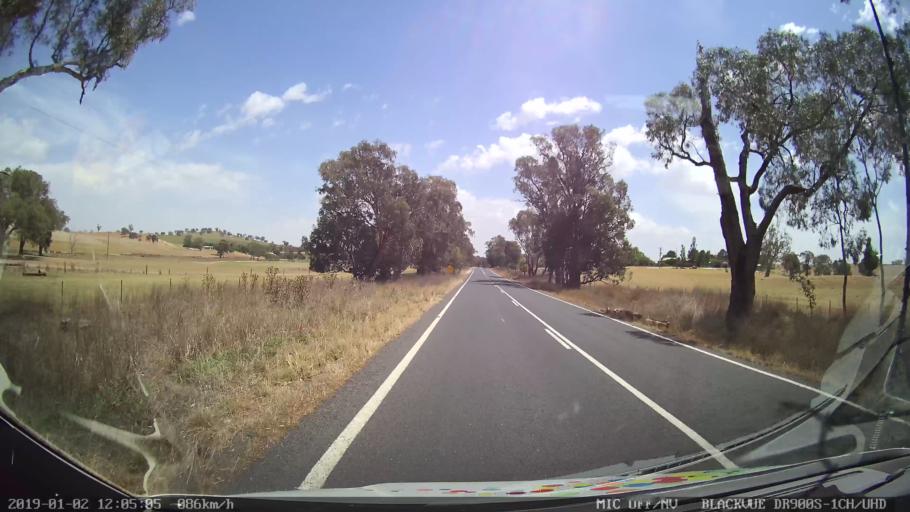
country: AU
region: New South Wales
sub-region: Young
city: Young
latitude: -34.5184
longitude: 148.3041
